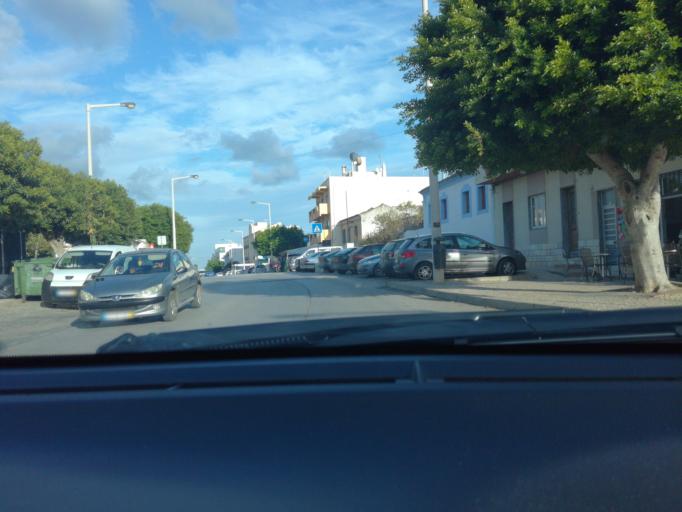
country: PT
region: Faro
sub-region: Olhao
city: Moncarapacho
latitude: 37.0832
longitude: -7.7901
